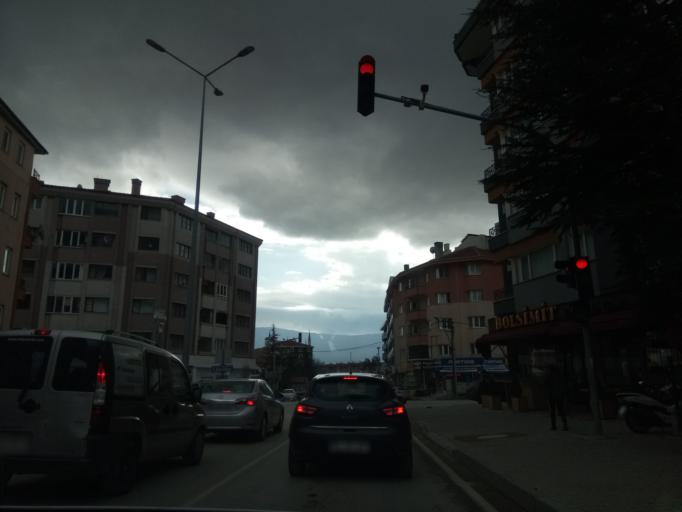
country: TR
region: Bolu
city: Bolu
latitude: 40.6920
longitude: 31.5360
